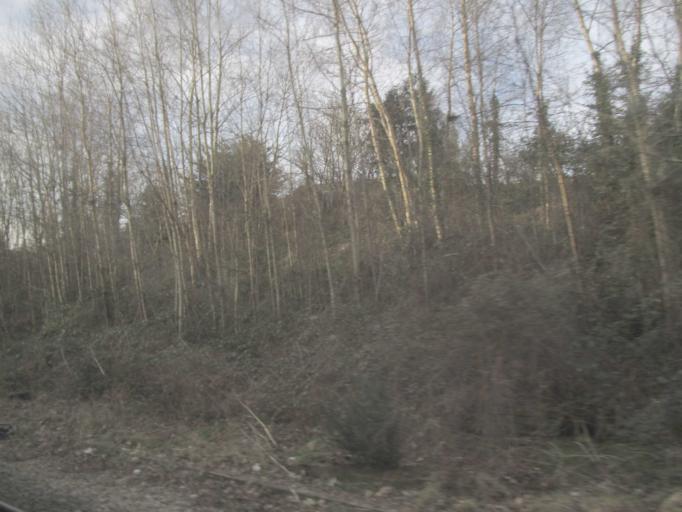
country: GB
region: England
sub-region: Wokingham
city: Wokingham
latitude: 51.4145
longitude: -0.8447
